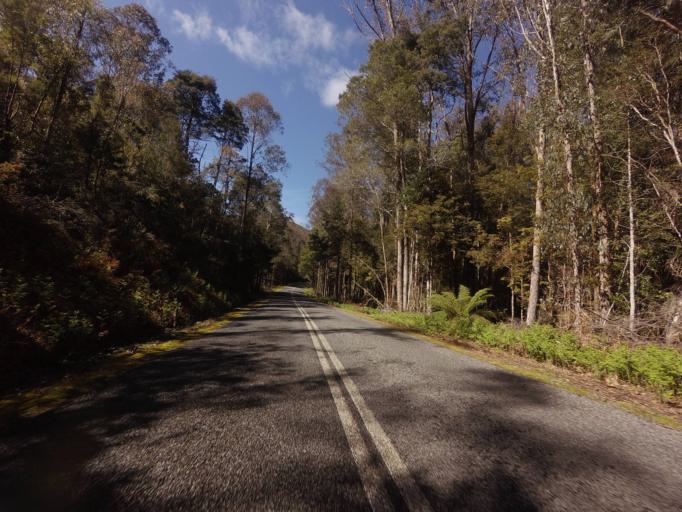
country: AU
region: Tasmania
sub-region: Huon Valley
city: Geeveston
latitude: -42.7764
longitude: 146.3977
